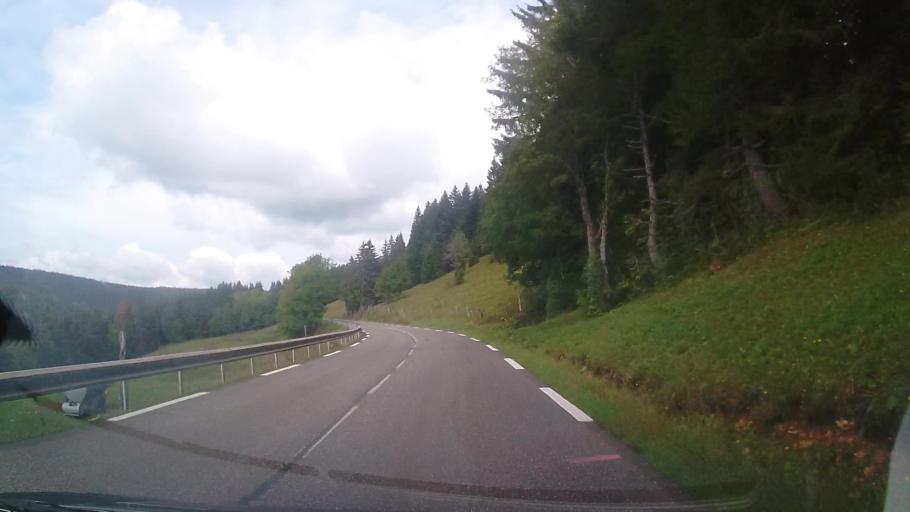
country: FR
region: Rhone-Alpes
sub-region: Departement de l'Ain
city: Gex
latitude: 46.3975
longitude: 6.0491
